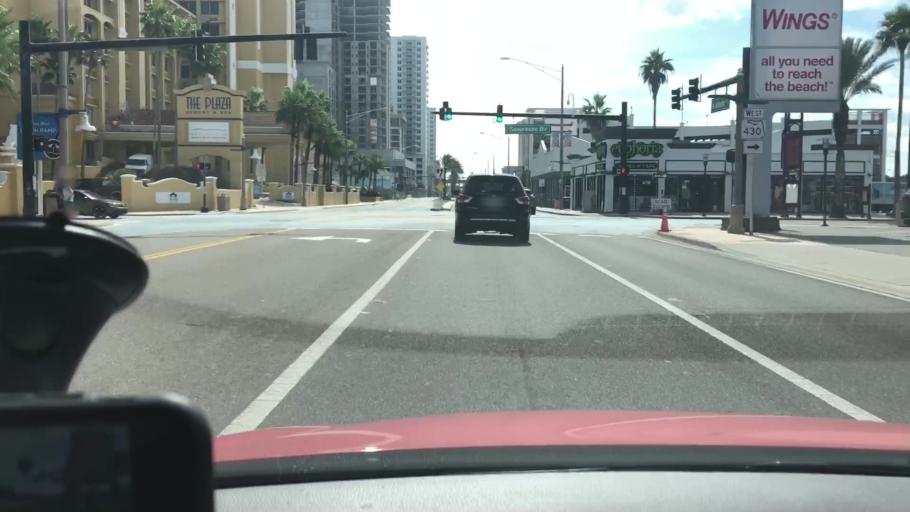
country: US
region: Florida
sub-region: Volusia County
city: Holly Hill
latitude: 29.2359
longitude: -81.0127
